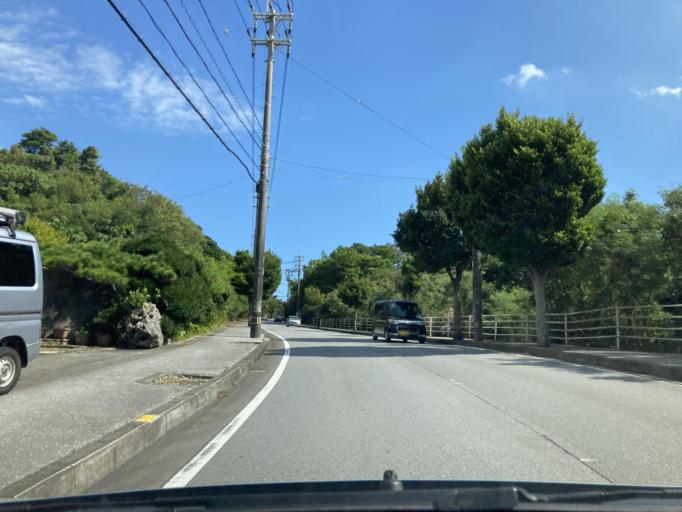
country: JP
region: Okinawa
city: Ginowan
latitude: 26.2438
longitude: 127.7561
